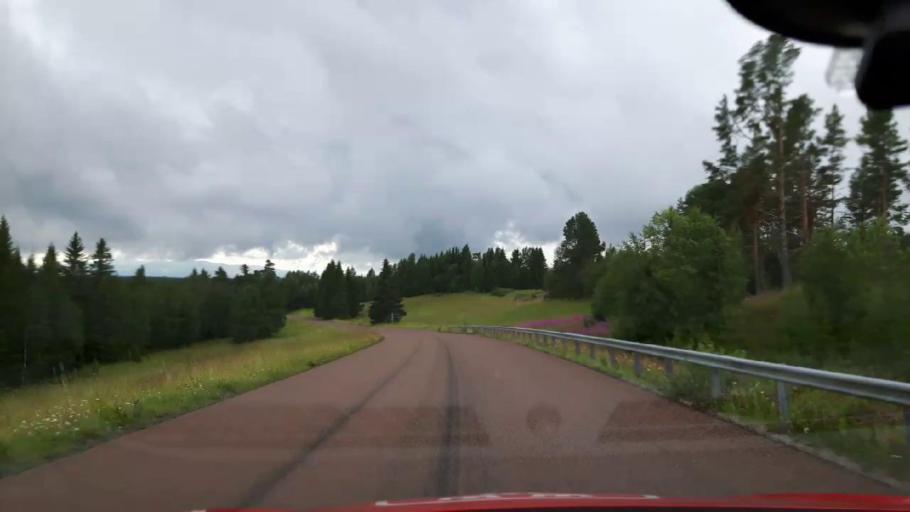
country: SE
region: Jaemtland
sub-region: Krokoms Kommun
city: Valla
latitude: 63.3499
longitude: 13.7227
